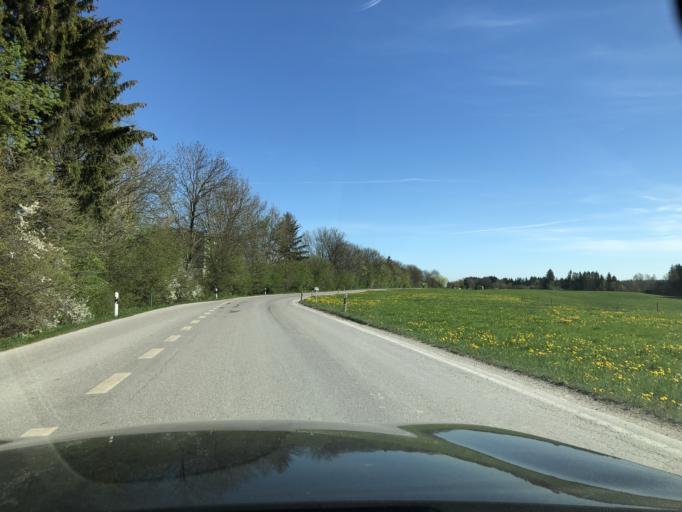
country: DE
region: Bavaria
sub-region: Swabia
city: Marktoberdorf
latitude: 47.7653
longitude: 10.5792
